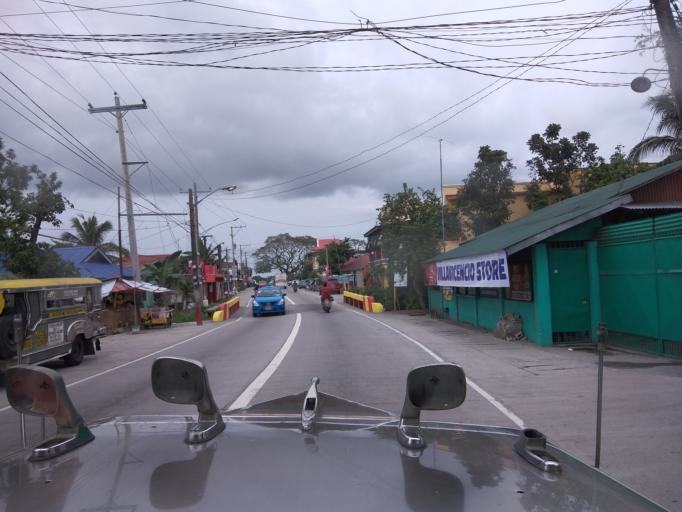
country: PH
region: Central Luzon
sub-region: Province of Pampanga
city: Pandacaqui
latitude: 15.1883
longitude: 120.6345
